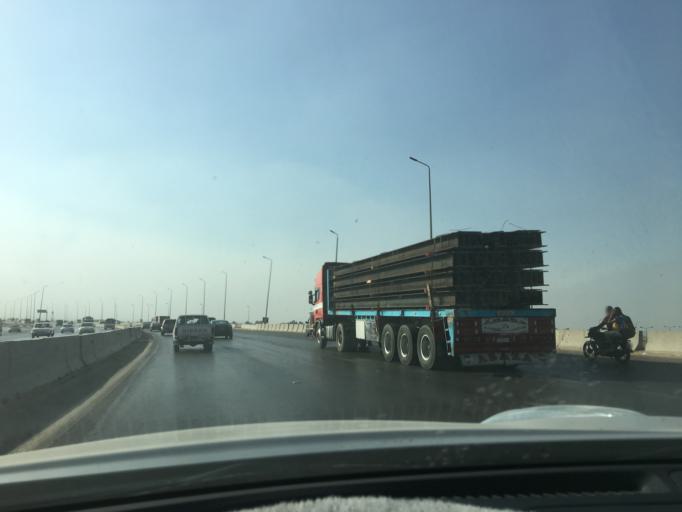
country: EG
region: Muhafazat al Qalyubiyah
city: Al Khankah
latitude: 30.1311
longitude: 31.4635
